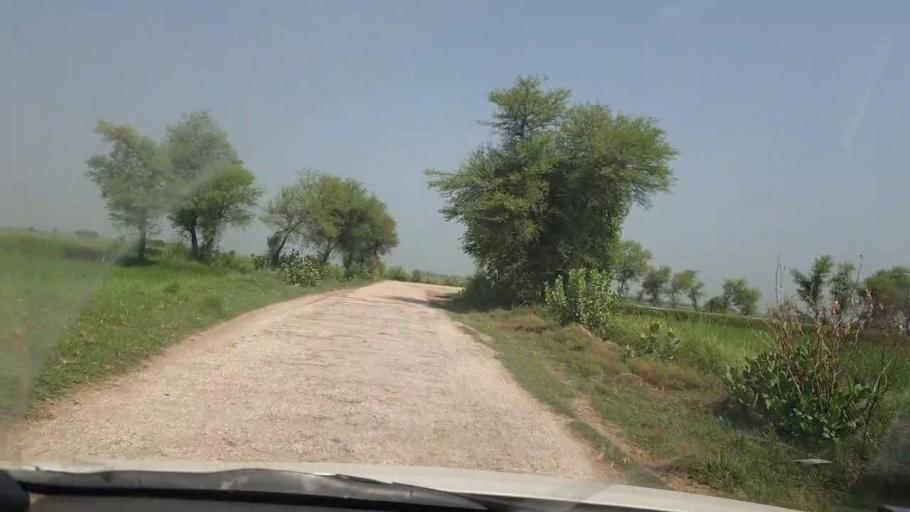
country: PK
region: Sindh
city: Chak
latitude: 27.8888
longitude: 68.7859
